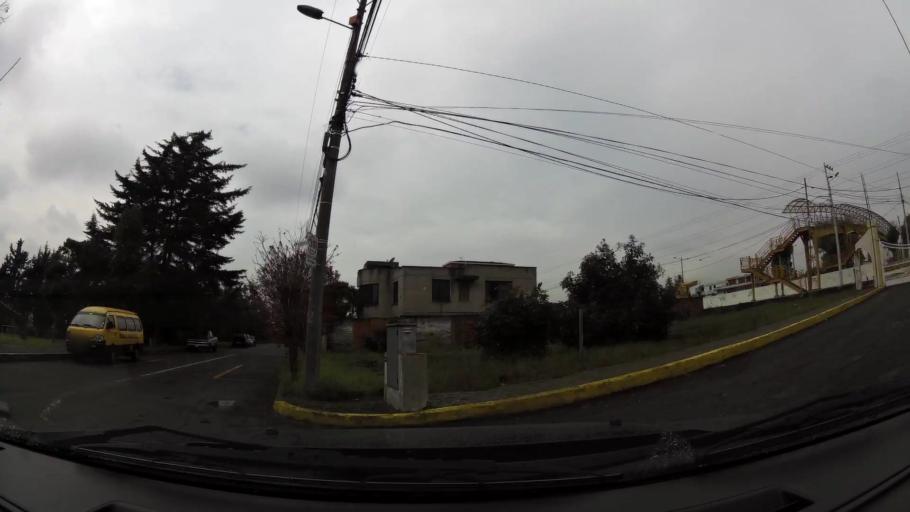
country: EC
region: Pichincha
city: Sangolqui
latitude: -0.2898
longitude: -78.4650
